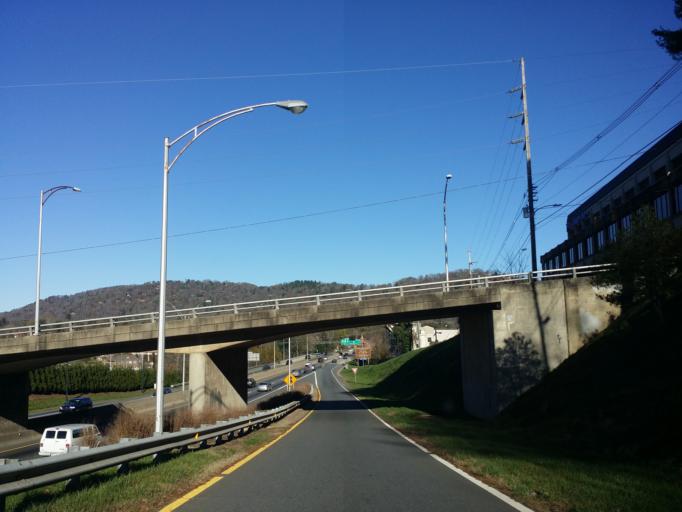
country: US
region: North Carolina
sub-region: Buncombe County
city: Asheville
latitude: 35.5977
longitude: -82.5567
